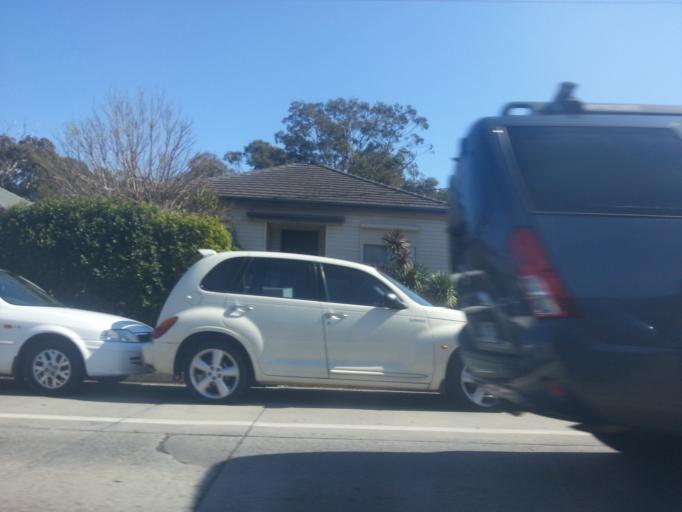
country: AU
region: New South Wales
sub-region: Wollongong
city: East Corrimal
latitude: -34.3776
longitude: 150.9084
